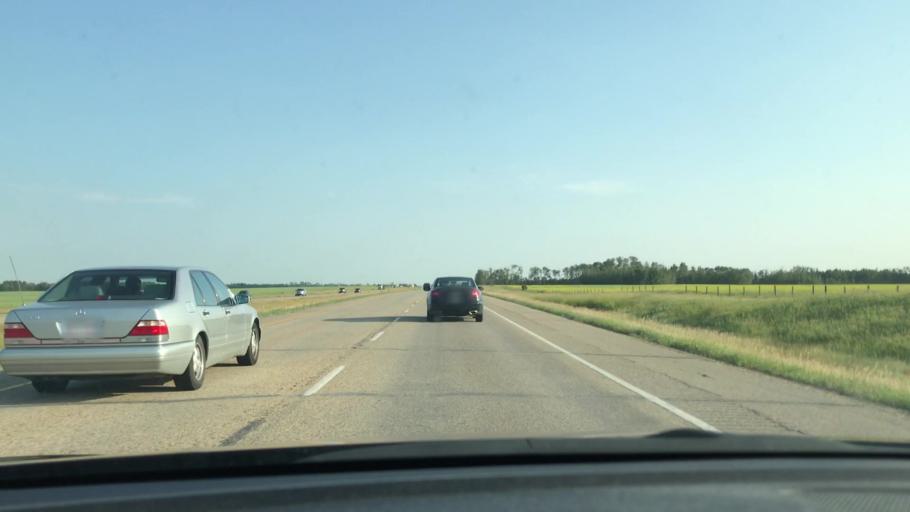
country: CA
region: Alberta
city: Millet
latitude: 53.1325
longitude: -113.5985
